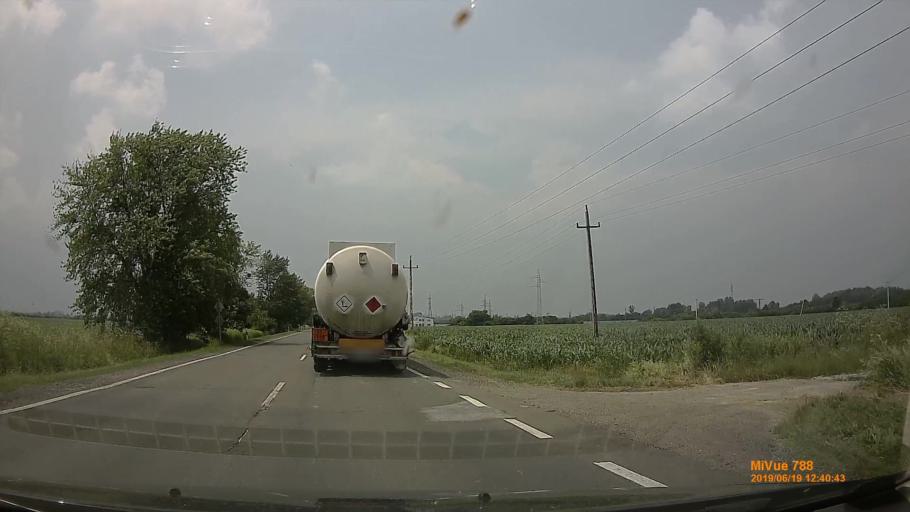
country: HU
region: Baranya
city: Szigetvar
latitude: 46.0494
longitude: 17.8360
